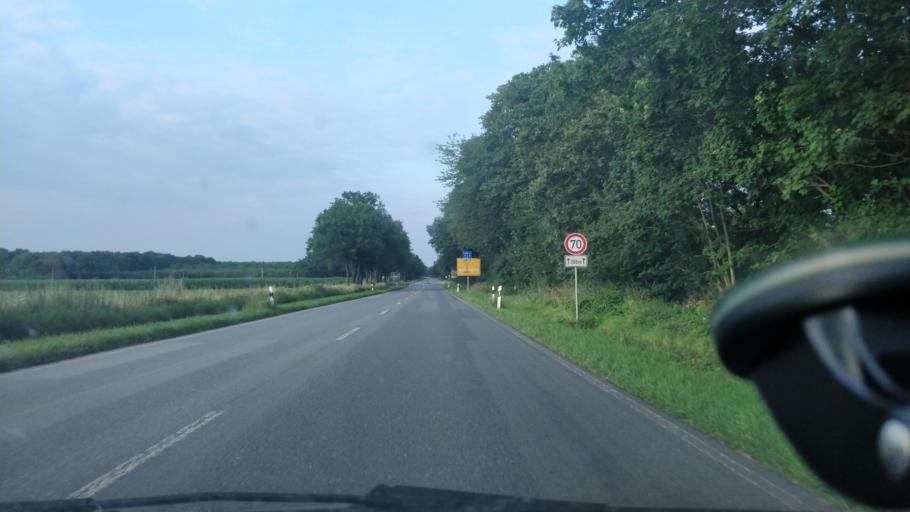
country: DE
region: North Rhine-Westphalia
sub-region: Regierungsbezirk Dusseldorf
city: Kamp-Lintfort
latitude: 51.5221
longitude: 6.5564
